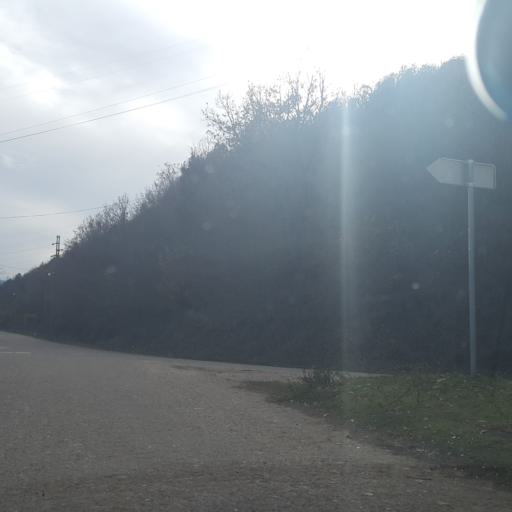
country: RS
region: Central Serbia
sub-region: Zajecarski Okrug
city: Knjazevac
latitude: 43.5817
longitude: 22.2477
